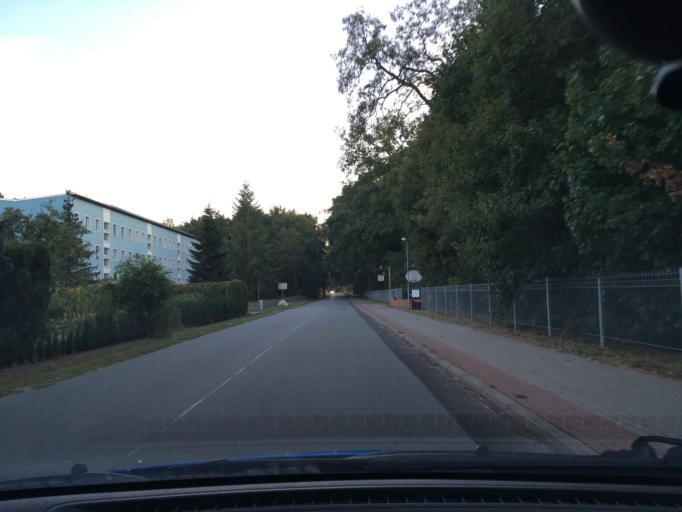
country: DE
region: Mecklenburg-Vorpommern
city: Boizenburg
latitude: 53.3969
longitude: 10.7459
